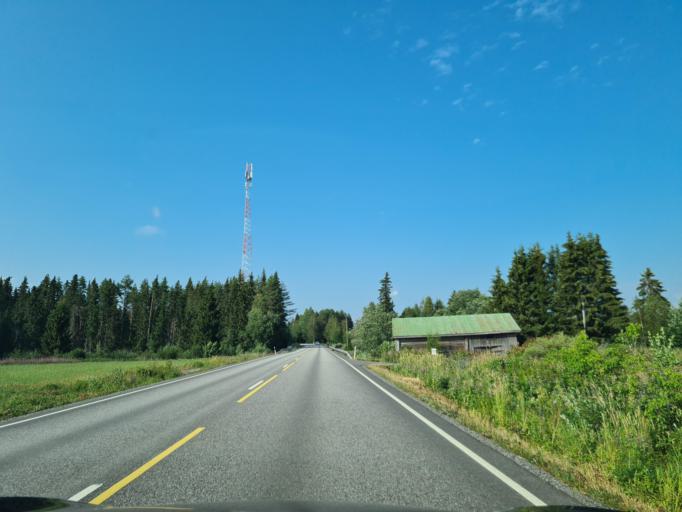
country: FI
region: Satakunta
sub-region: Pohjois-Satakunta
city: Kankaanpaeae
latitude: 61.9409
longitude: 22.5104
